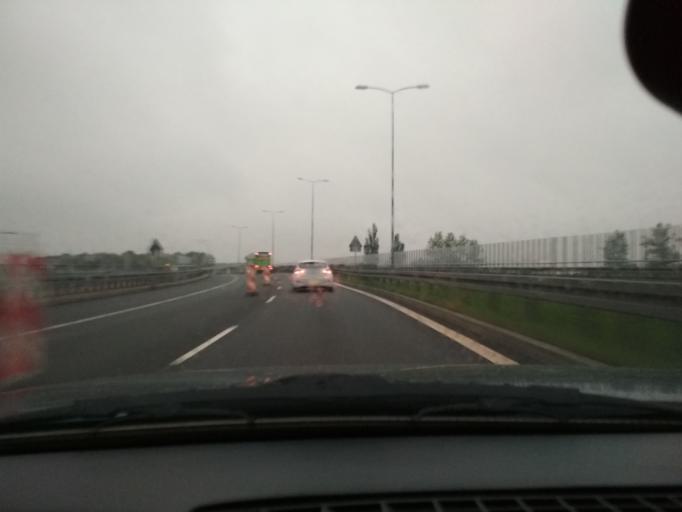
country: PL
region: Silesian Voivodeship
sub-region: Zabrze
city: Zabrze
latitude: 50.2911
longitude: 18.7856
